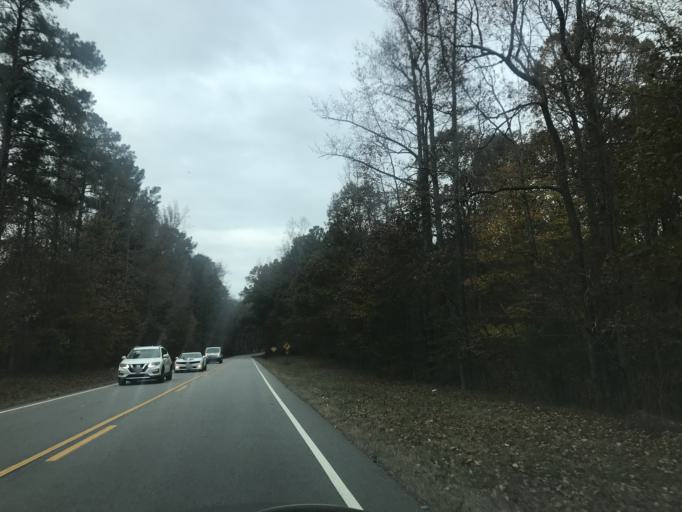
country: US
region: North Carolina
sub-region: Franklin County
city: Youngsville
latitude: 36.0117
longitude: -78.4910
